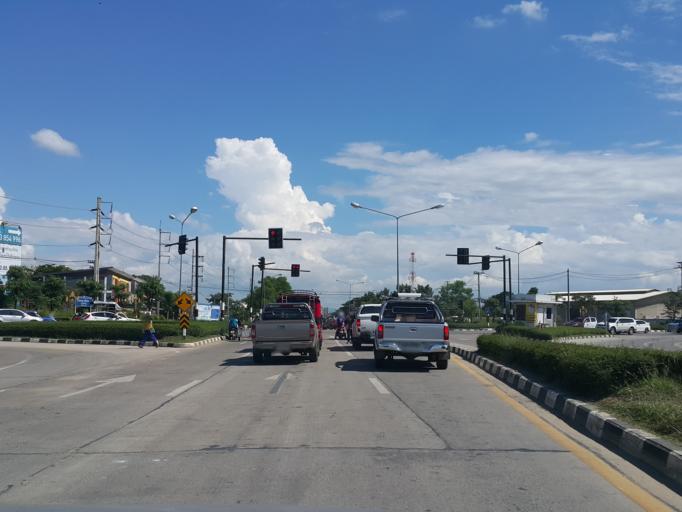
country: TH
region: Chiang Mai
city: San Sai
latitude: 18.8476
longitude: 99.0131
